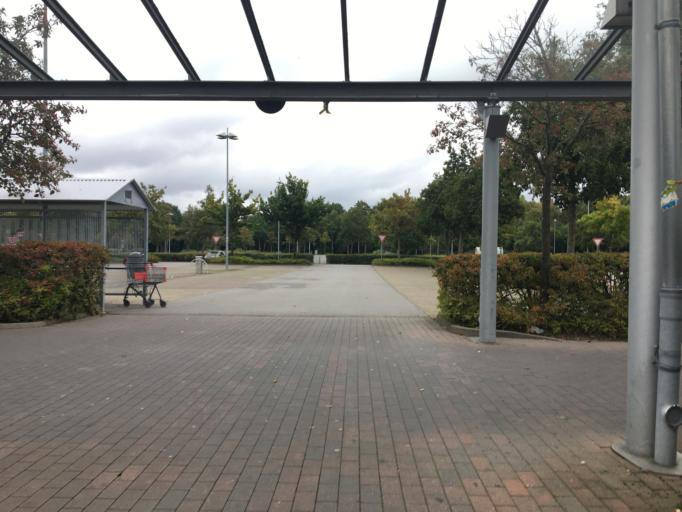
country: DE
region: Mecklenburg-Vorpommern
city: Kramerhof
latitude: 54.3205
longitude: 13.0487
